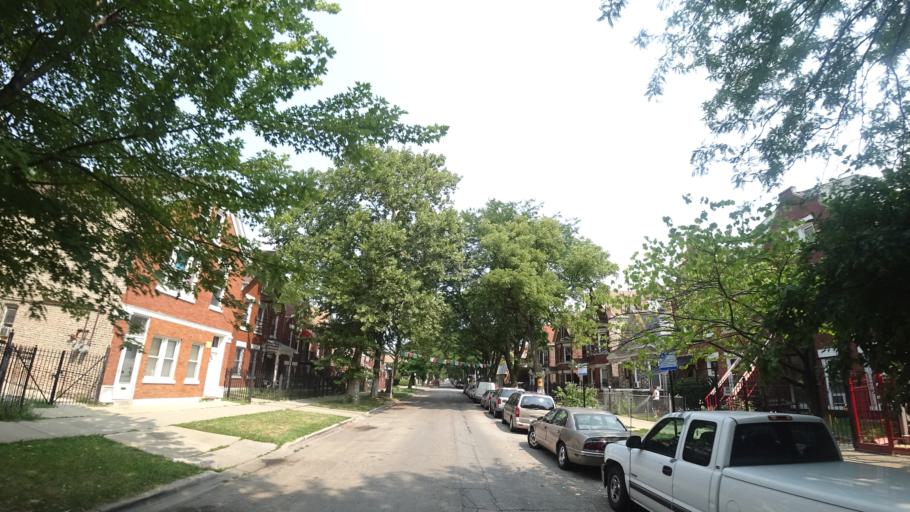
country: US
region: Illinois
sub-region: Cook County
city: Cicero
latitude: 41.8398
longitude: -87.7208
